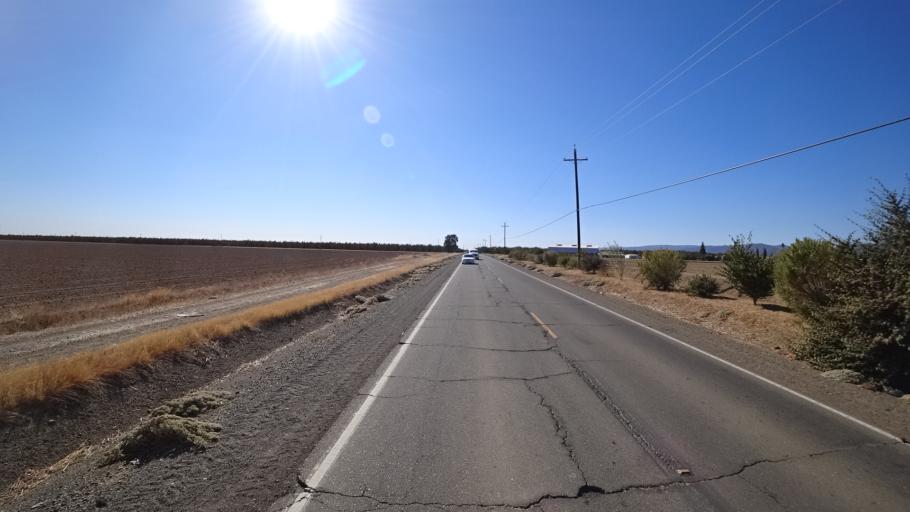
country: US
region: California
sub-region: Yolo County
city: Winters
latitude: 38.5870
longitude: -121.9714
